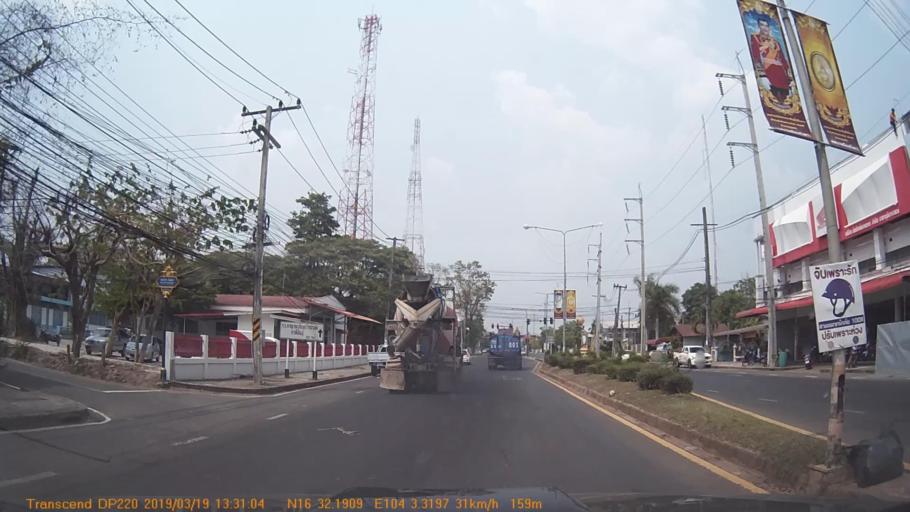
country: TH
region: Kalasin
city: Kuchinarai
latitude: 16.5366
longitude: 104.0553
